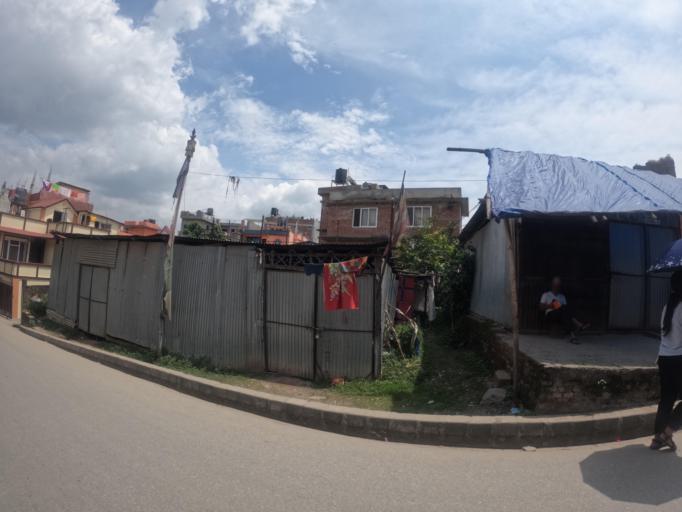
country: NP
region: Central Region
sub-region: Bagmati Zone
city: Patan
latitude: 27.6758
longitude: 85.3658
